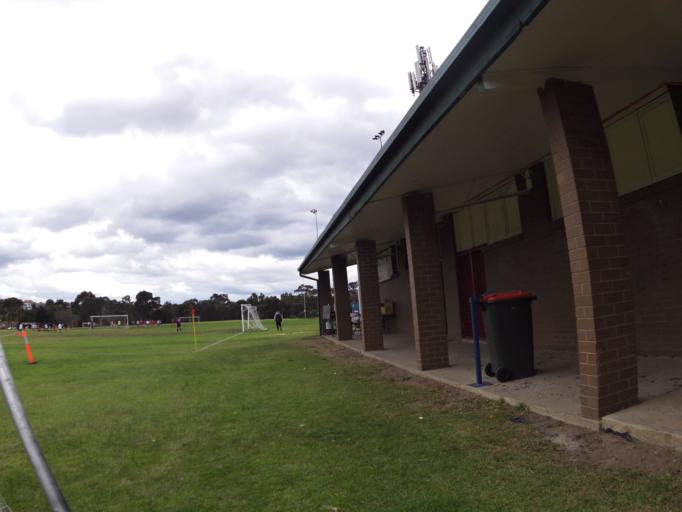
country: AU
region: Victoria
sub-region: Moreland
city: Pascoe Vale
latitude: -37.7449
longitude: 144.9295
